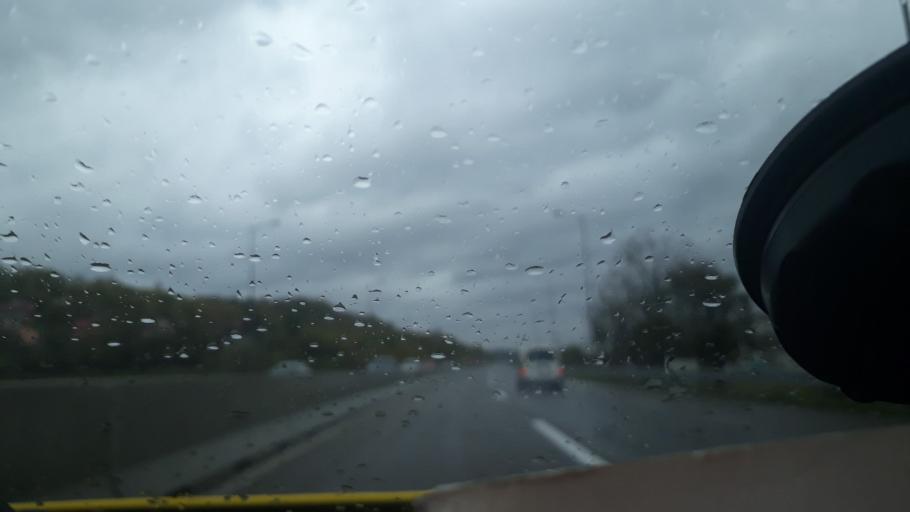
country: BA
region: Republika Srpska
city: Trn
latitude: 44.8714
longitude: 17.2623
